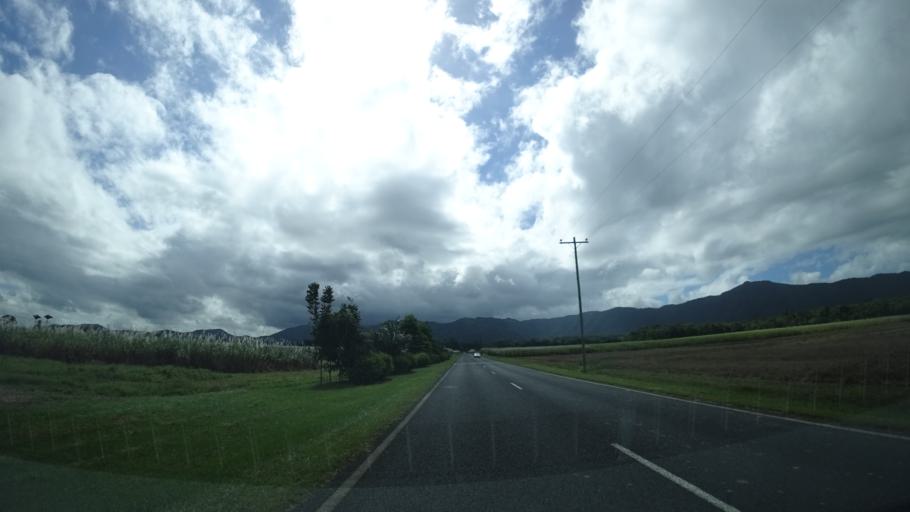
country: AU
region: Queensland
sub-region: Cairns
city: Port Douglas
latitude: -16.2673
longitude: 145.3924
